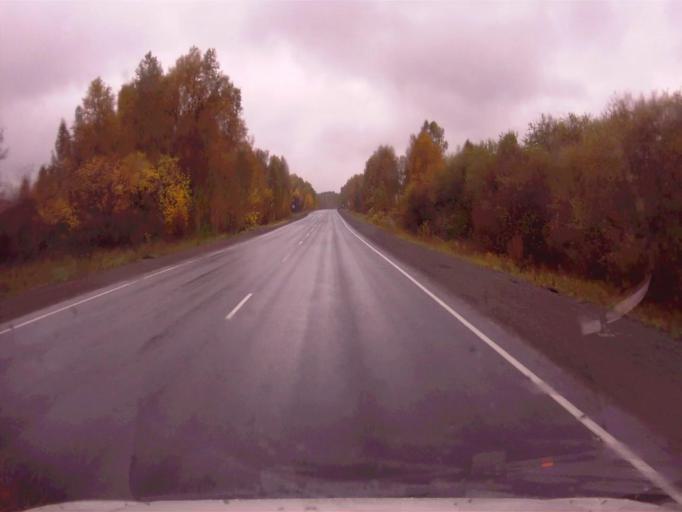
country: RU
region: Chelyabinsk
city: Argayash
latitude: 55.4785
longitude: 60.7793
